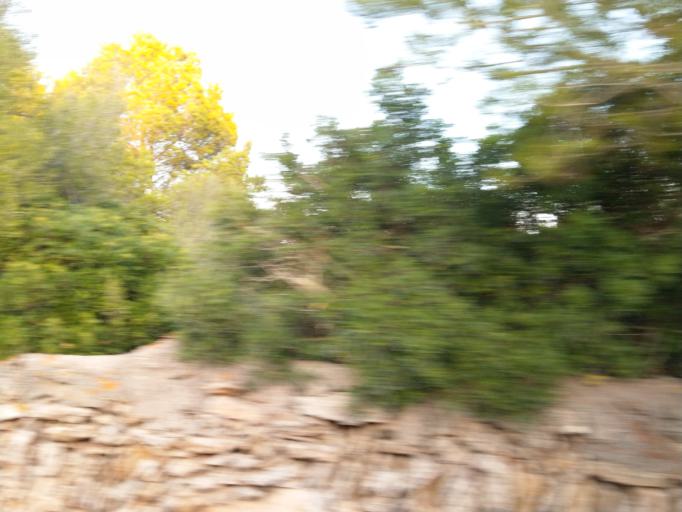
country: ES
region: Balearic Islands
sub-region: Illes Balears
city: Santanyi
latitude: 39.3152
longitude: 3.1194
